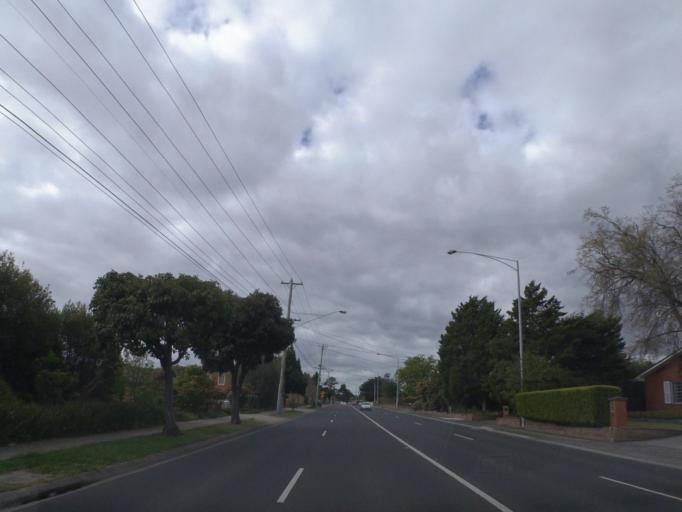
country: AU
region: Victoria
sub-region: Manningham
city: Doncaster
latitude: -37.7809
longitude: 145.1114
